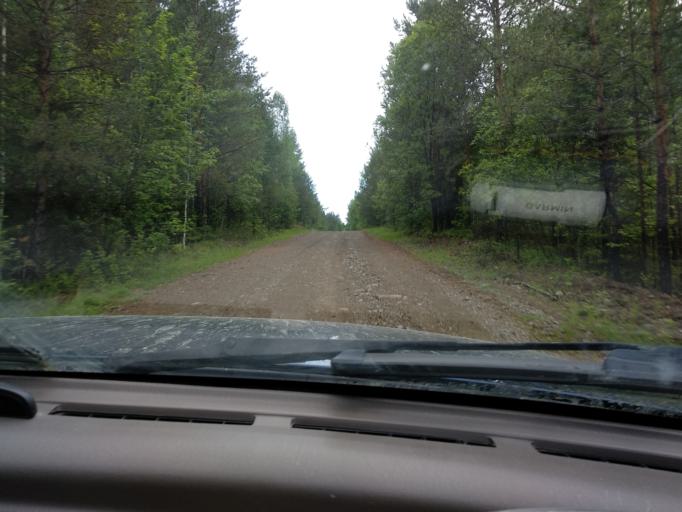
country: RU
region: Sverdlovsk
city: Karpinsk
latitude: 59.3990
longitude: 59.9482
